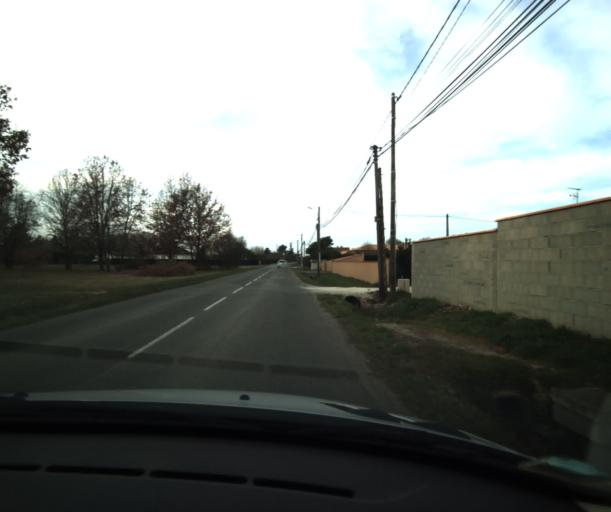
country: FR
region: Midi-Pyrenees
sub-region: Departement du Tarn-et-Garonne
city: Montech
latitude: 43.9432
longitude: 1.2372
